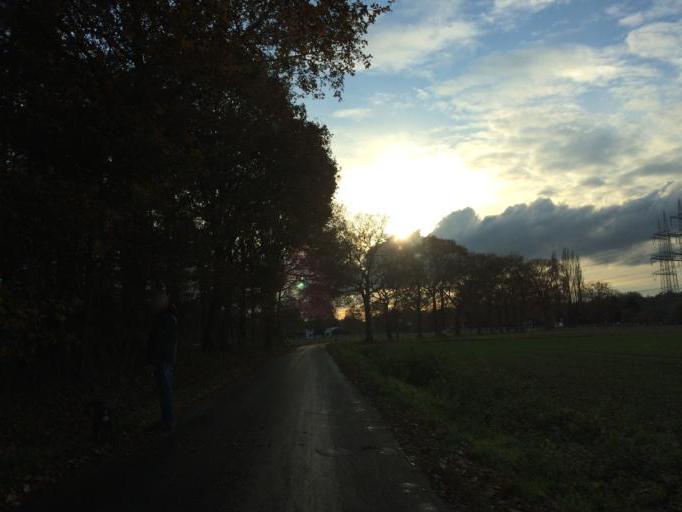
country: DE
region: North Rhine-Westphalia
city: Marl
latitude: 51.6721
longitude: 7.0667
